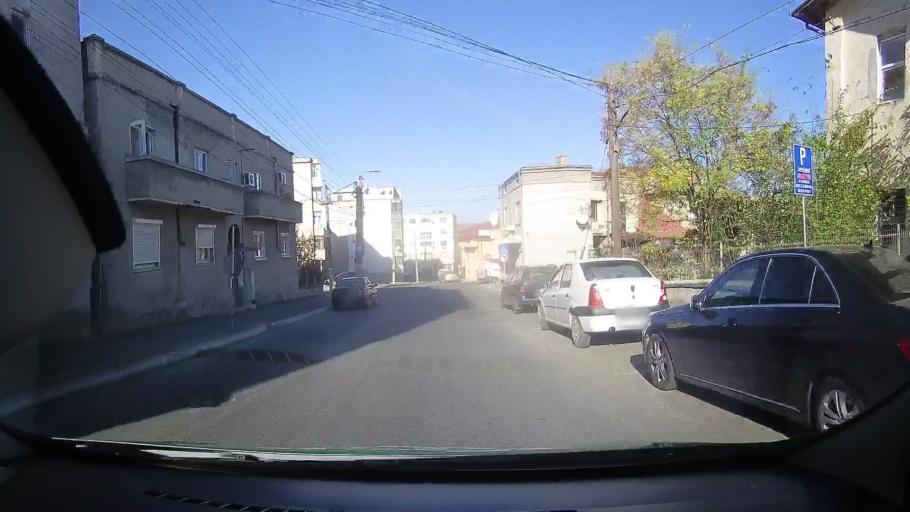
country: RO
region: Tulcea
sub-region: Oras Babadag
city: Babadag
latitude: 44.8934
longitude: 28.7255
